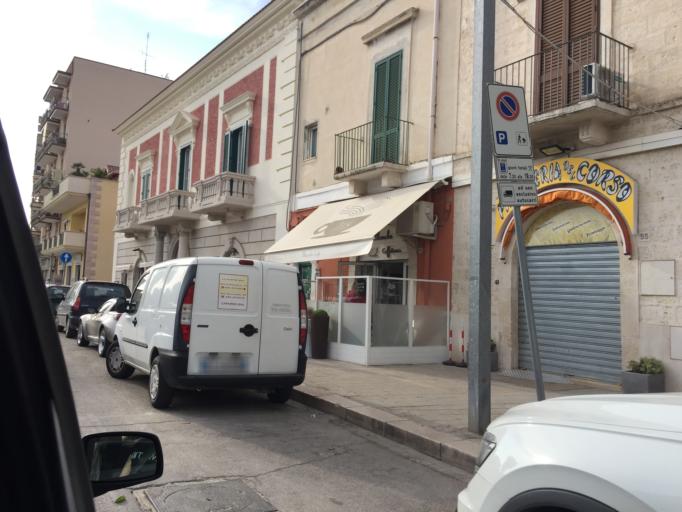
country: IT
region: Apulia
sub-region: Provincia di Bari
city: Capurso
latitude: 41.0486
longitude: 16.9205
